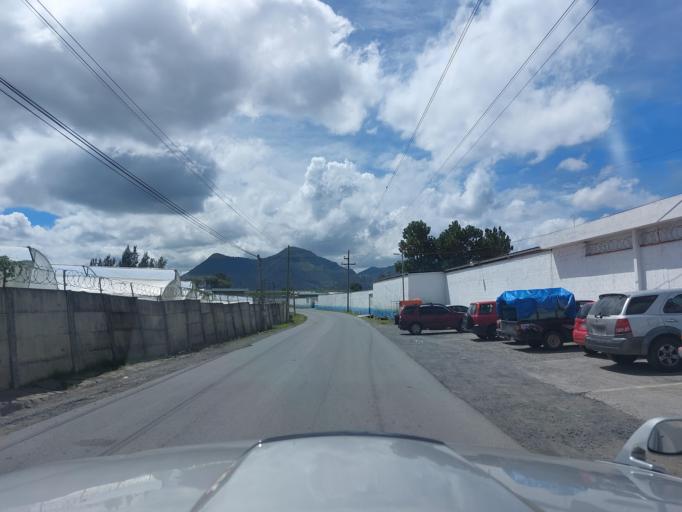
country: GT
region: Chimaltenango
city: Parramos
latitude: 14.6102
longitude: -90.8144
